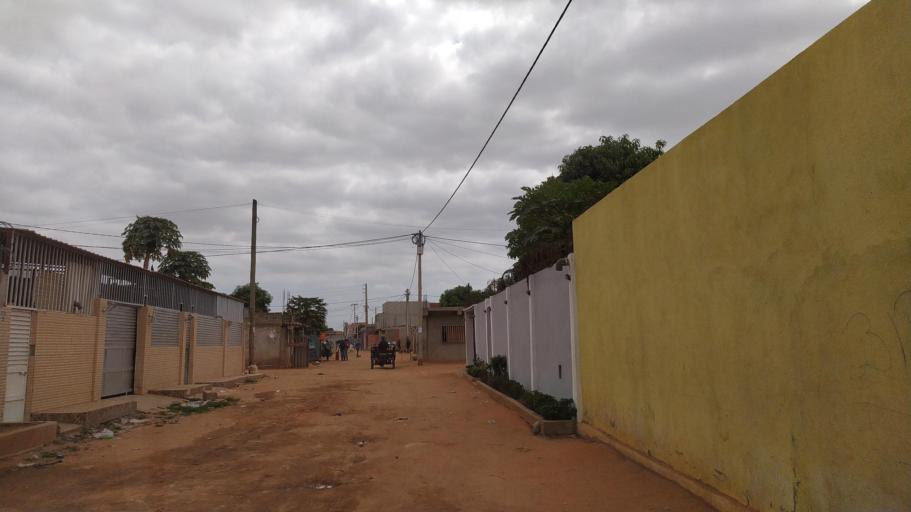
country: AO
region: Luanda
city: Luanda
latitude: -8.9339
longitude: 13.2569
